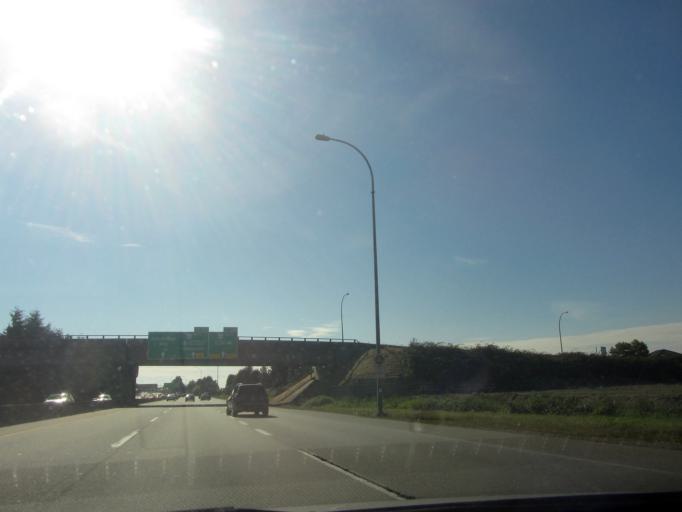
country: CA
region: British Columbia
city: Richmond
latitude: 49.1776
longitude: -123.0796
